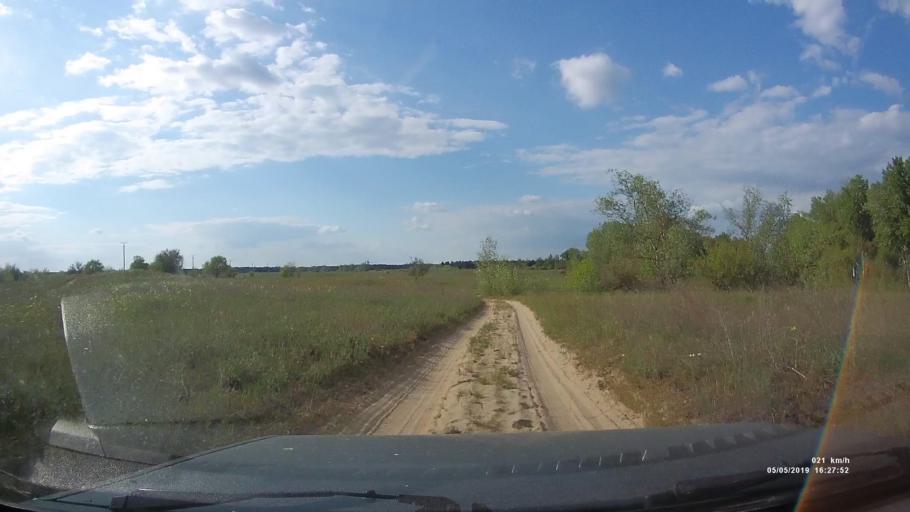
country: RU
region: Rostov
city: Ust'-Donetskiy
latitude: 47.7656
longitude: 41.0167
